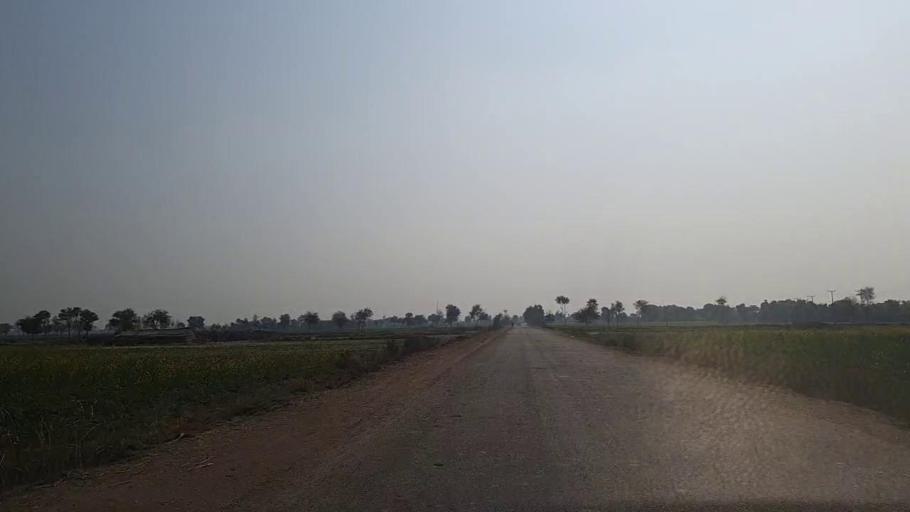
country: PK
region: Sindh
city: Jam Sahib
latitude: 26.3460
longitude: 68.5343
